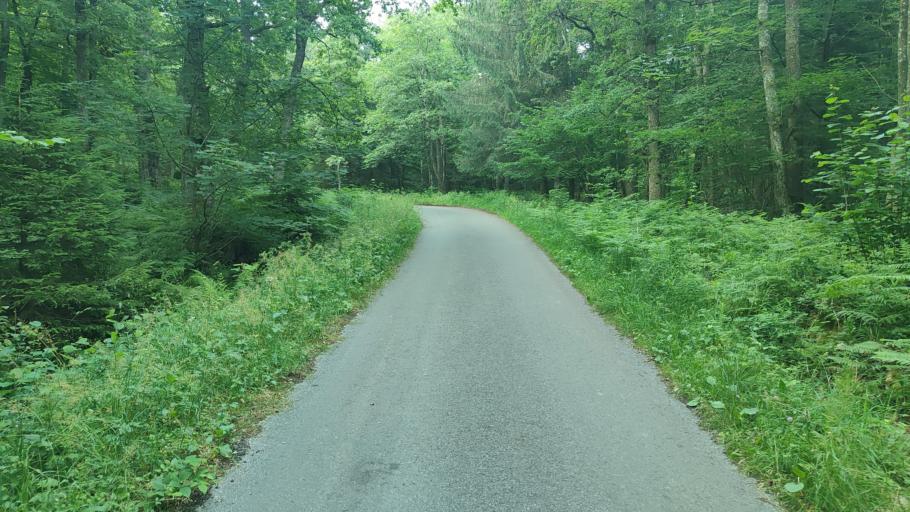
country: DE
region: North Rhine-Westphalia
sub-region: Regierungsbezirk Koln
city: Roetgen
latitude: 50.6203
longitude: 6.1785
